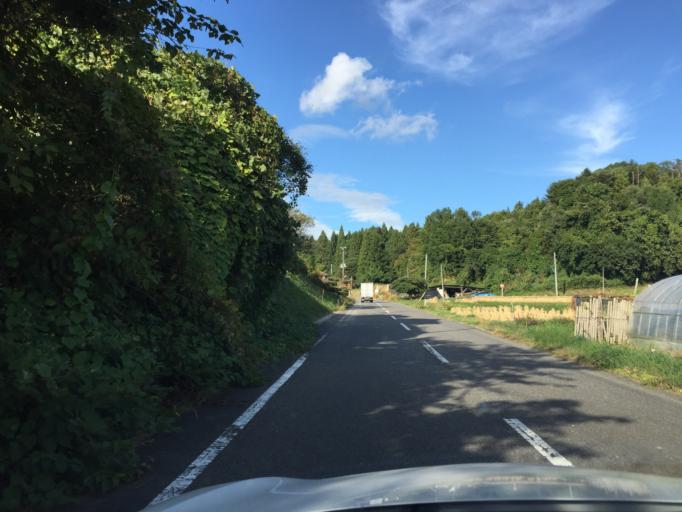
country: JP
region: Fukushima
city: Ishikawa
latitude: 37.2231
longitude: 140.4531
